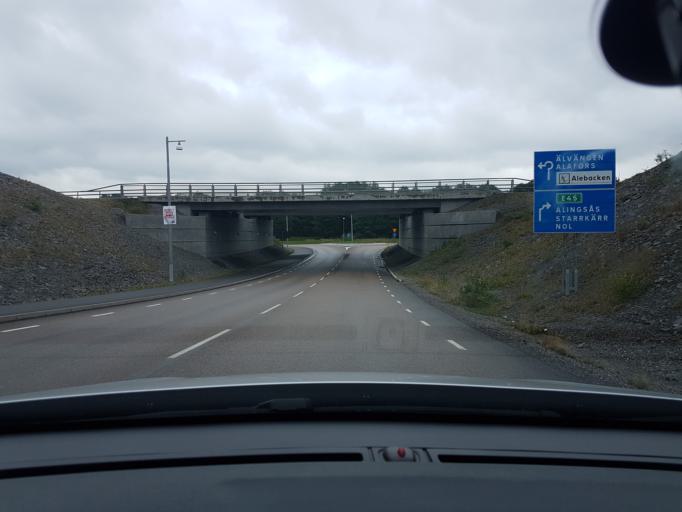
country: SE
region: Vaestra Goetaland
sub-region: Ale Kommun
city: Alafors
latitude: 57.9272
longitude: 12.0788
